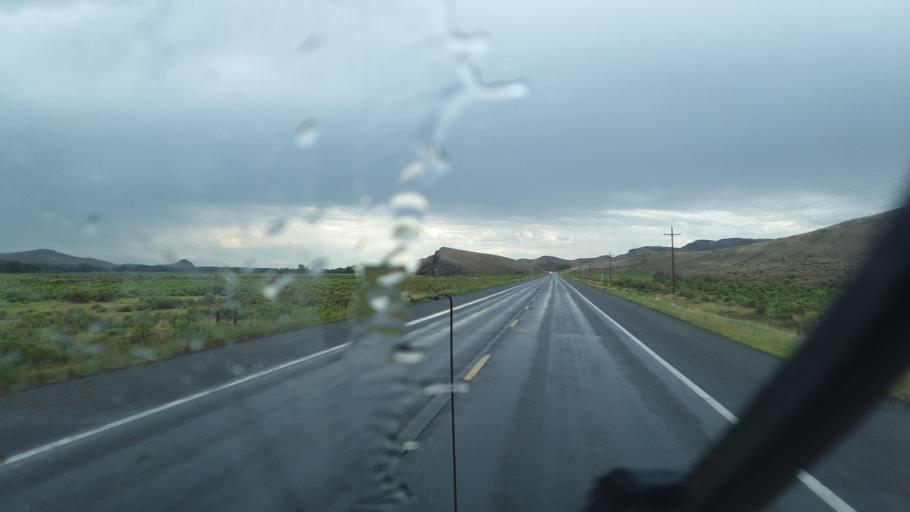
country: US
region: Colorado
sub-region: Rio Grande County
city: Del Norte
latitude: 37.6756
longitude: -106.4266
